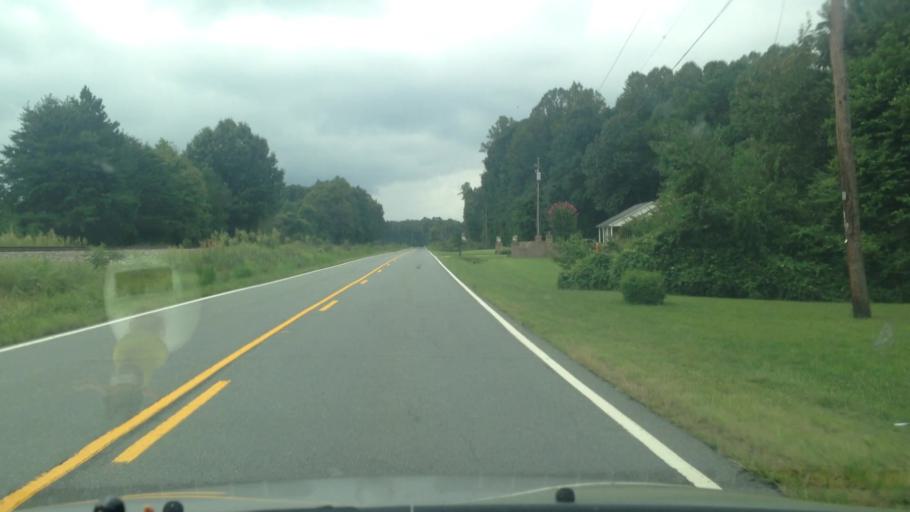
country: US
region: North Carolina
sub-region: Stokes County
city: Walnut Cove
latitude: 36.2543
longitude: -80.1485
